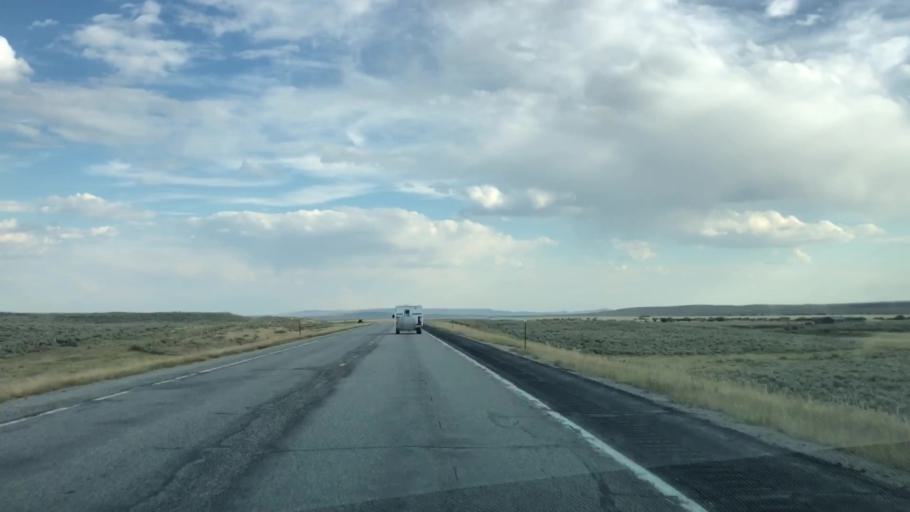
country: US
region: Wyoming
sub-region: Sublette County
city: Pinedale
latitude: 43.0501
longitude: -110.1512
